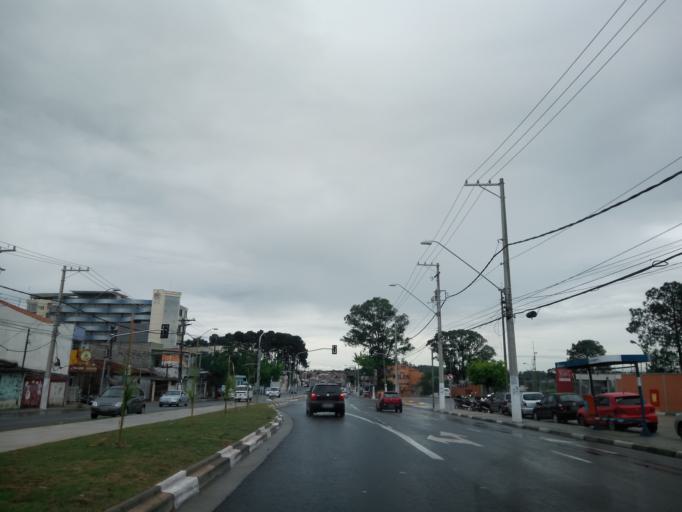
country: BR
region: Sao Paulo
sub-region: Sao Bernardo Do Campo
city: Sao Bernardo do Campo
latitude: -23.7304
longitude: -46.5783
